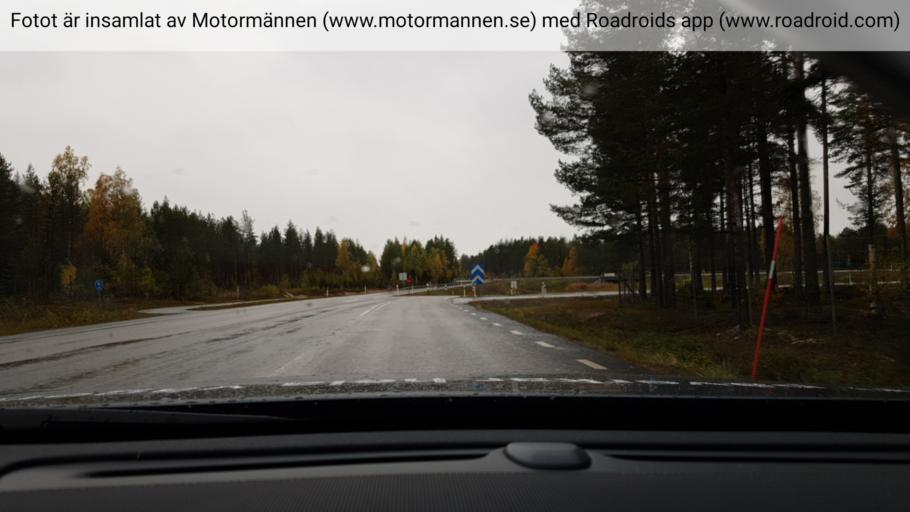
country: SE
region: Norrbotten
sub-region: Lulea Kommun
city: Gammelstad
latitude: 65.5822
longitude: 22.0012
